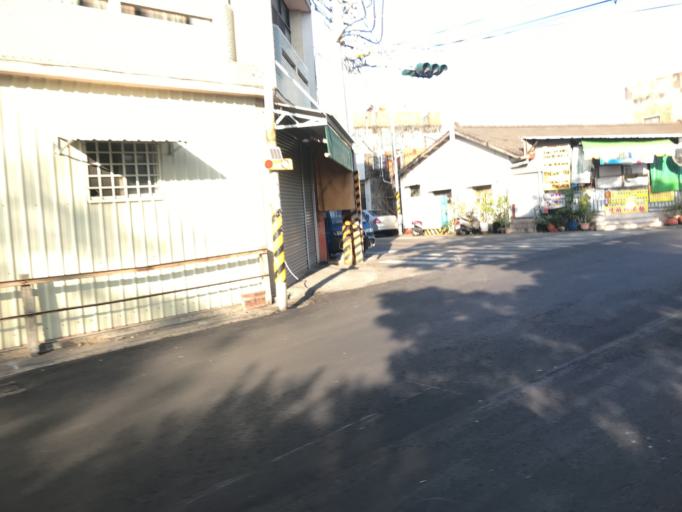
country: TW
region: Taiwan
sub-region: Nantou
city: Nantou
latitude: 23.8967
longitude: 120.5944
